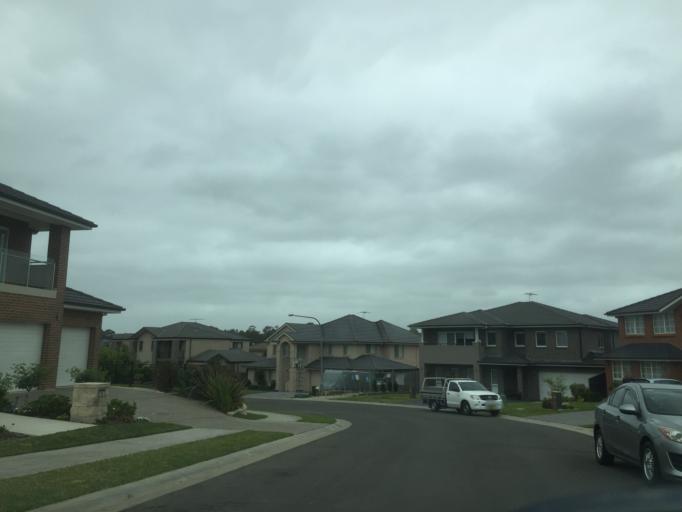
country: AU
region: New South Wales
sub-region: The Hills Shire
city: Beaumont Hills
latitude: -33.7207
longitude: 150.9537
